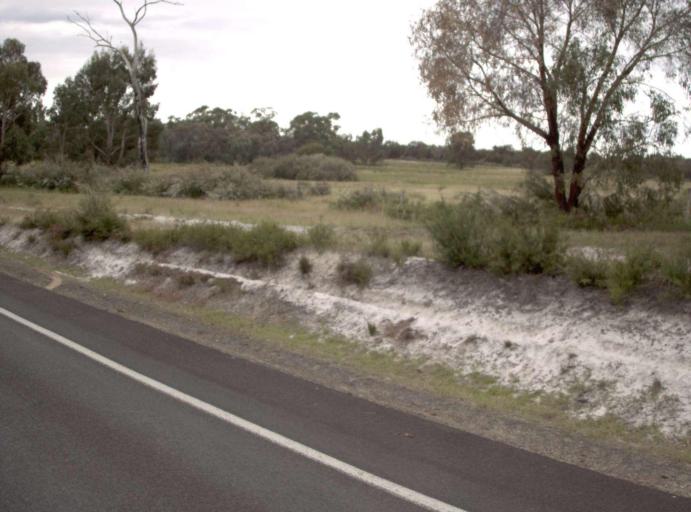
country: AU
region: Victoria
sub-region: Wellington
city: Sale
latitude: -38.3418
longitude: 147.0050
